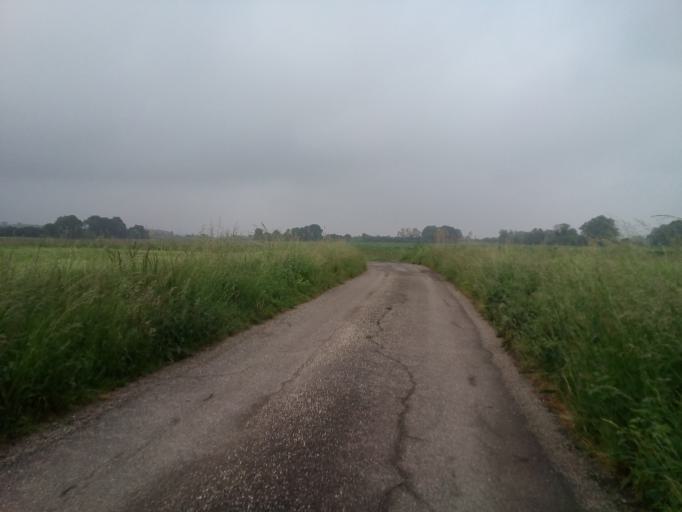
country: DE
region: Baden-Wuerttemberg
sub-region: Freiburg Region
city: Rheinau
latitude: 48.6850
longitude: 7.9587
